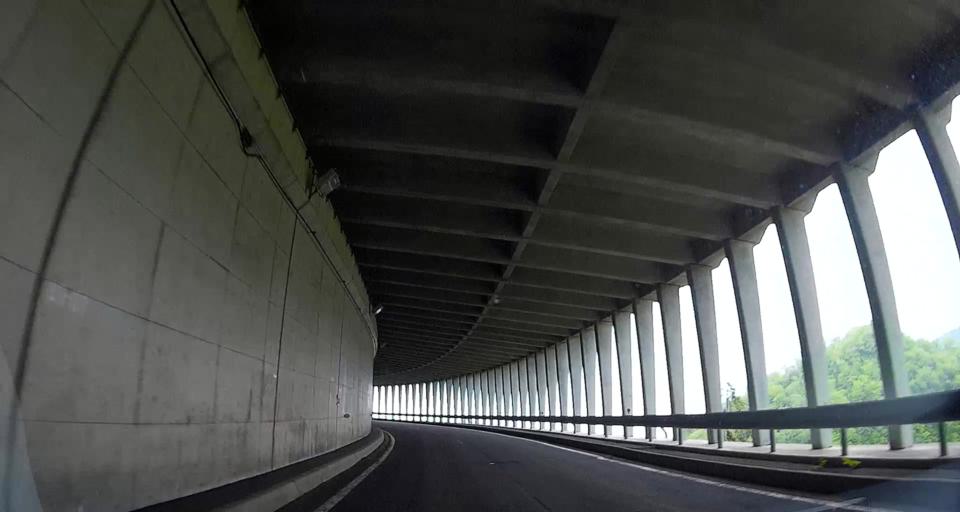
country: JP
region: Hokkaido
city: Shiraoi
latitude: 42.6581
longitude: 141.1739
